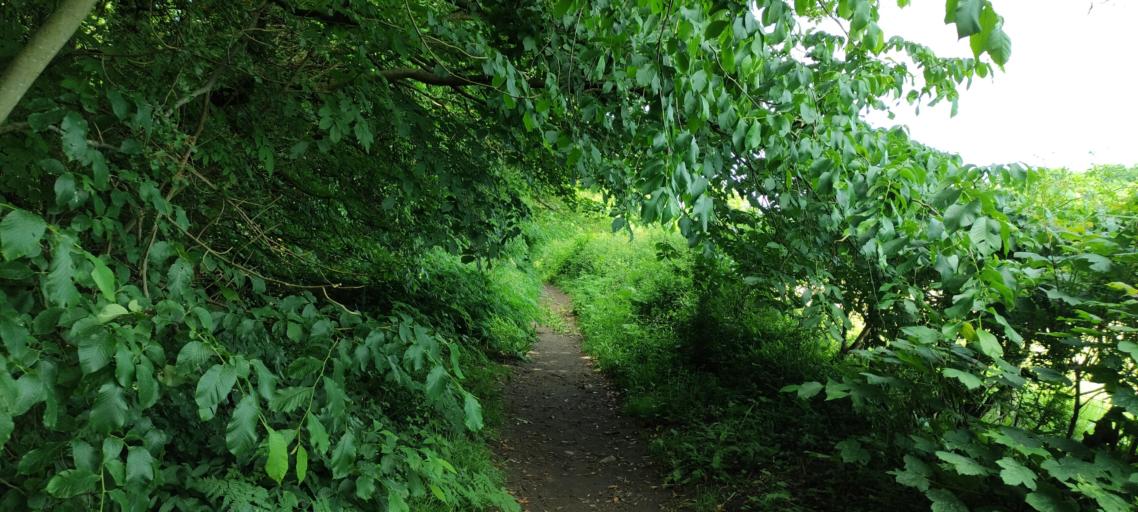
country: GB
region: England
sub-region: North Yorkshire
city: Bedale
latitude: 54.2139
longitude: -1.6527
